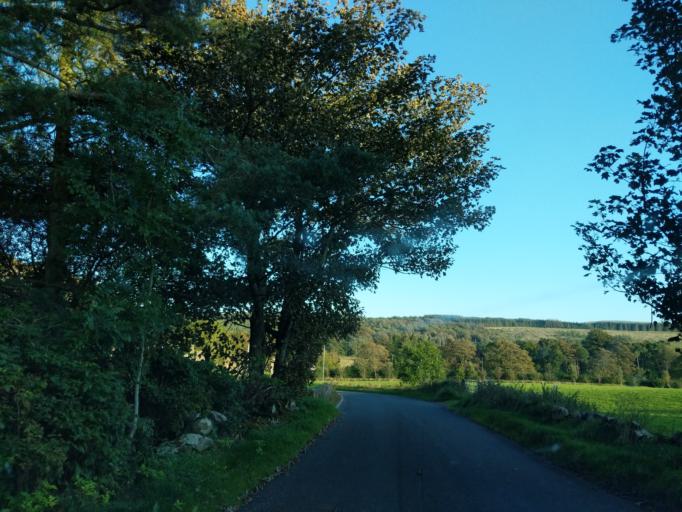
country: GB
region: Scotland
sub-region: The Scottish Borders
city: West Linton
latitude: 55.7029
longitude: -3.4329
